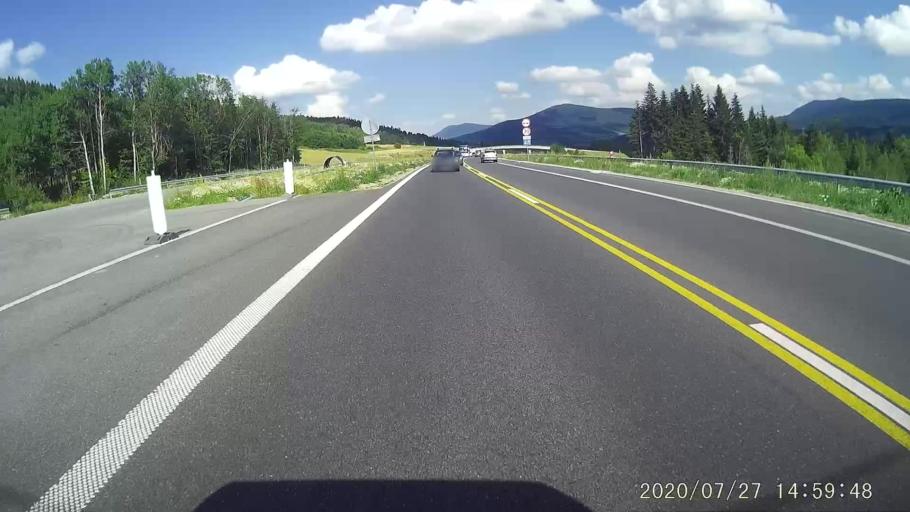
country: PL
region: Lesser Poland Voivodeship
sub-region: Powiat suski
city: Letownia
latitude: 49.6951
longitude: 19.9101
